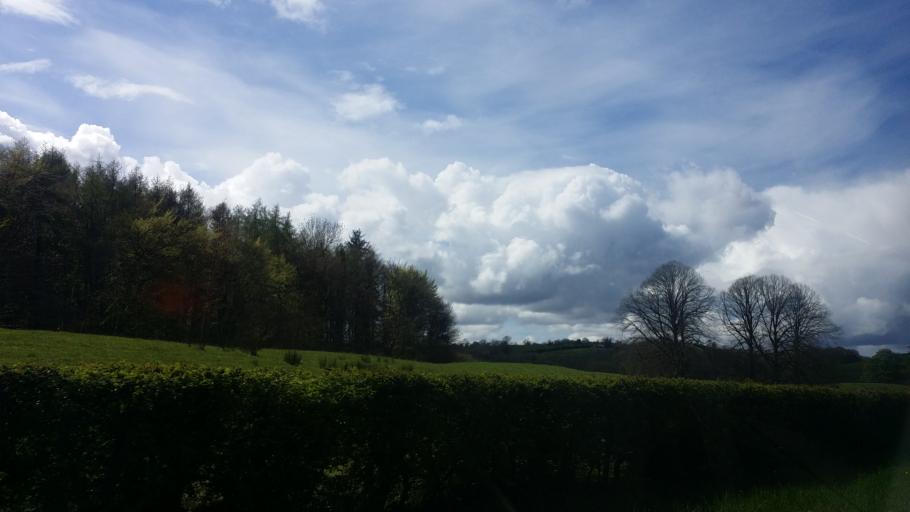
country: GB
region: Northern Ireland
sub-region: Fermanagh District
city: Enniskillen
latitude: 54.3836
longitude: -7.6933
